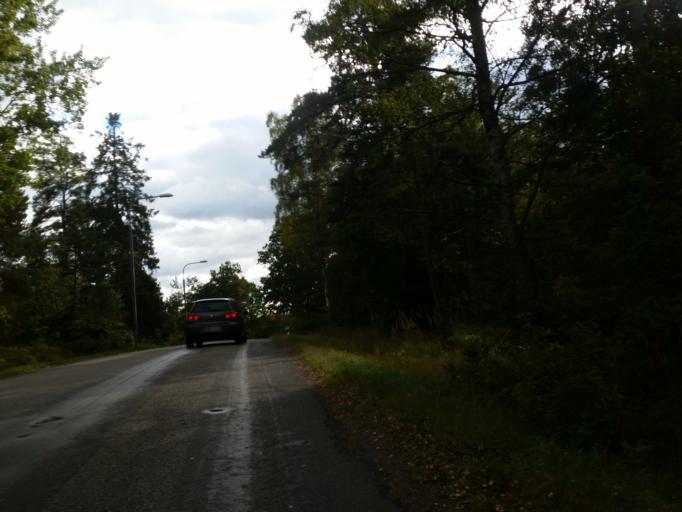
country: SE
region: Stockholm
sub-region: Nacka Kommun
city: Alta
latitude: 59.2508
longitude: 18.1362
